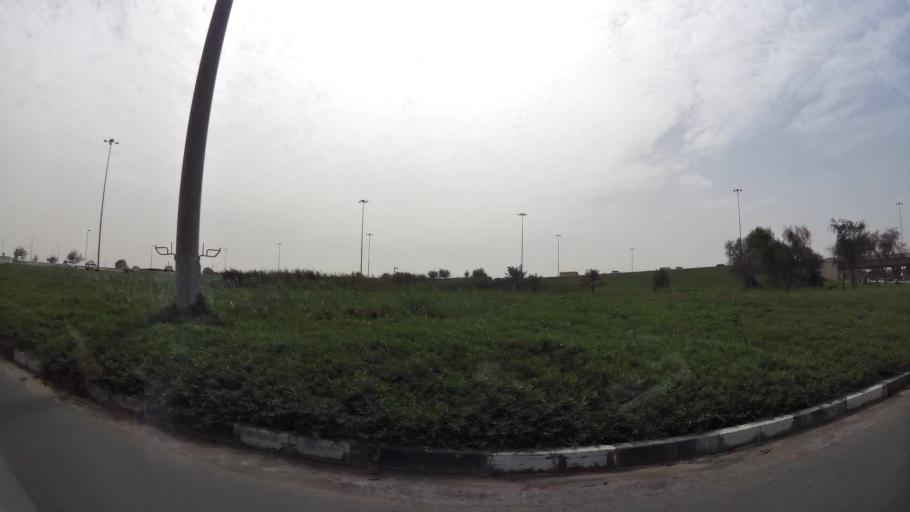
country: AE
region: Abu Dhabi
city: Abu Dhabi
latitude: 24.3974
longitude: 54.5763
